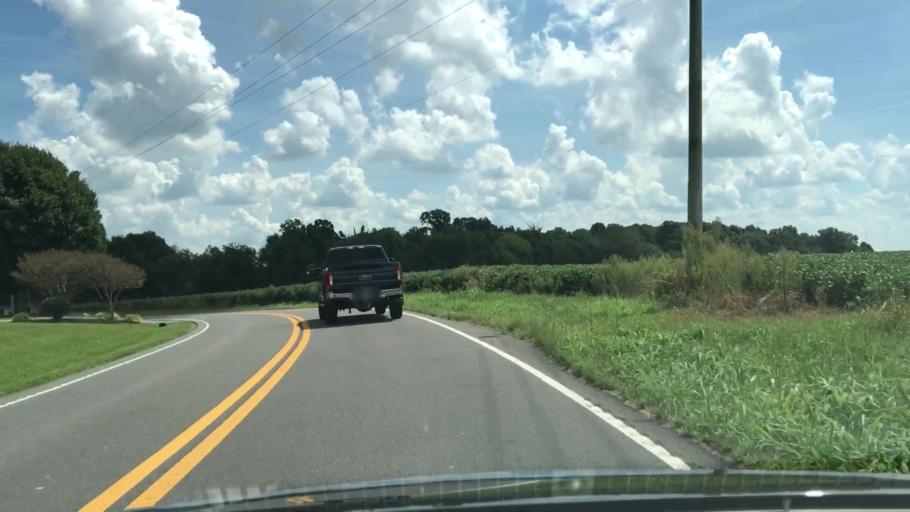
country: US
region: Tennessee
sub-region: Robertson County
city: Springfield
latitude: 36.5554
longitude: -86.8258
